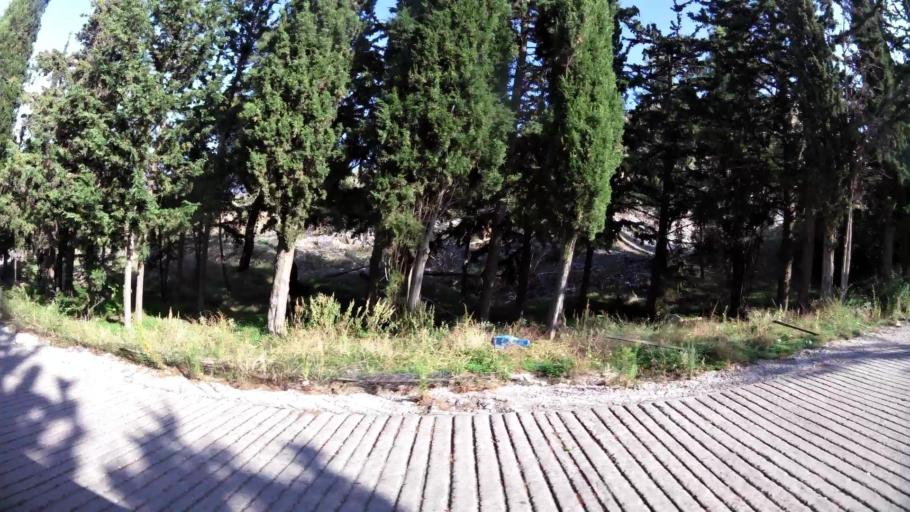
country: GR
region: Attica
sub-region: Nomarchia Athinas
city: Ilioupoli
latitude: 37.9431
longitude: 23.7752
